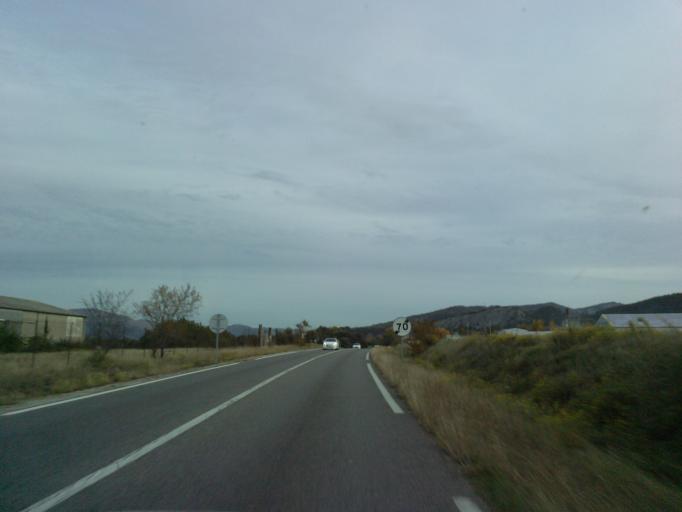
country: FR
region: Provence-Alpes-Cote d'Azur
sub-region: Departement des Alpes-de-Haute-Provence
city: Peipin
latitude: 44.1374
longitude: 5.9692
